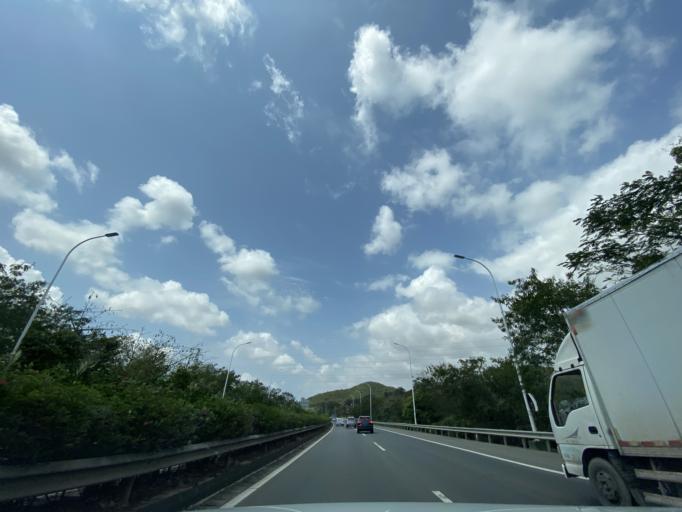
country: CN
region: Hainan
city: Tiandu
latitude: 18.3213
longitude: 109.5587
